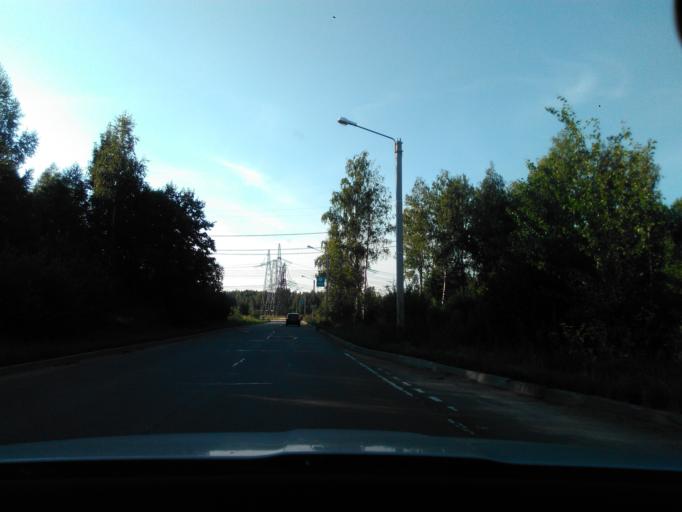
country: RU
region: Tverskaya
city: Konakovo
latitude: 56.7436
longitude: 36.7783
